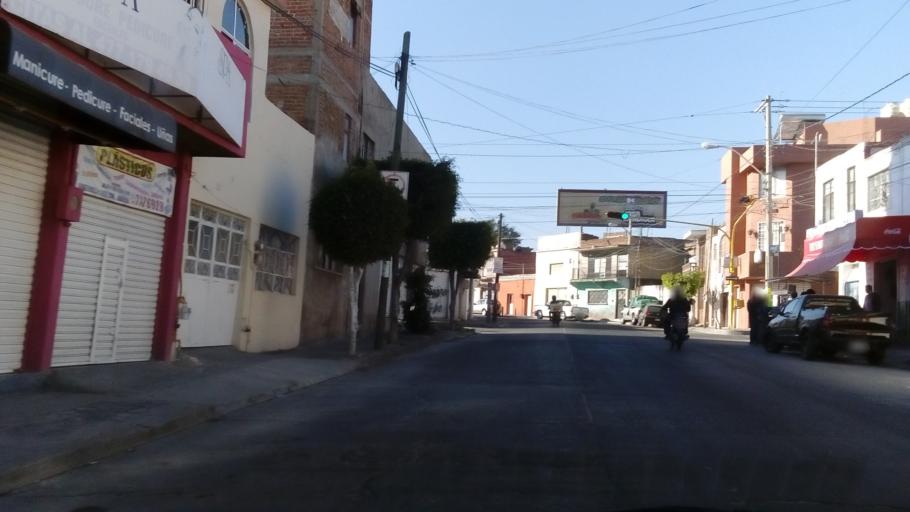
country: MX
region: Guanajuato
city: Leon
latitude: 21.1270
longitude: -101.6938
